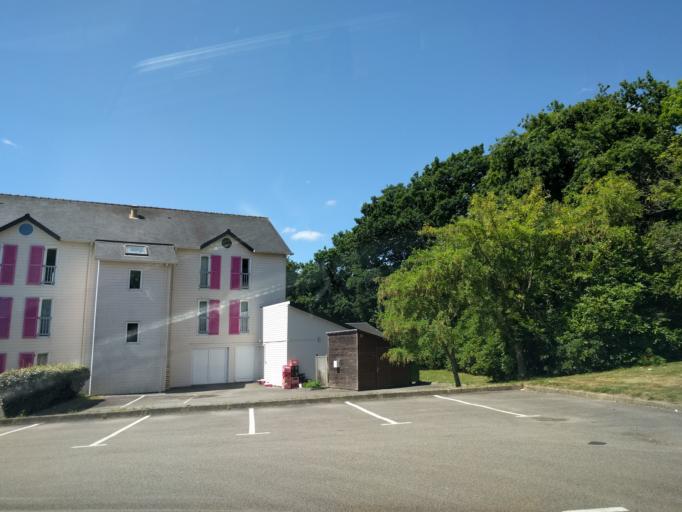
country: FR
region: Brittany
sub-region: Departement du Finistere
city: Quimper
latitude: 47.9798
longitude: -4.1022
